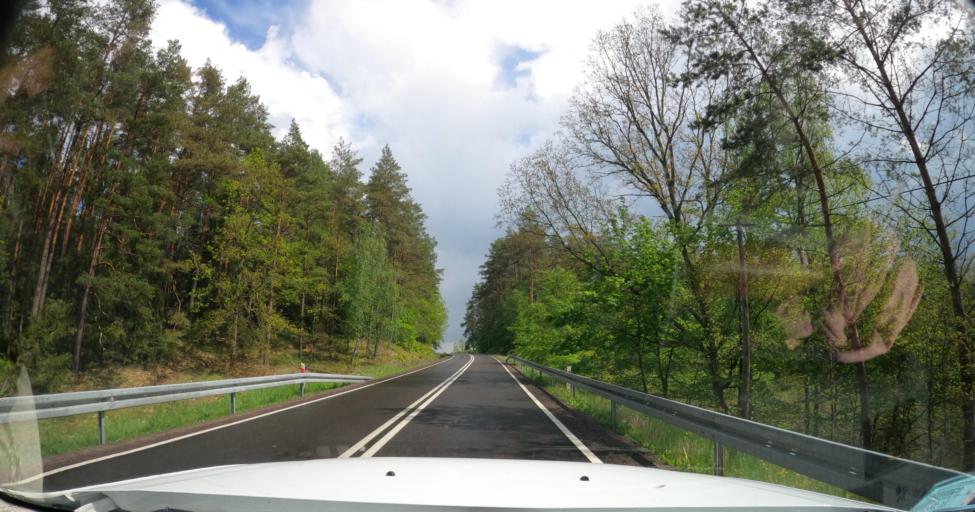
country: PL
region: Pomeranian Voivodeship
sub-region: Powiat bytowski
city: Czarna Dabrowka
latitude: 54.3402
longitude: 17.6169
